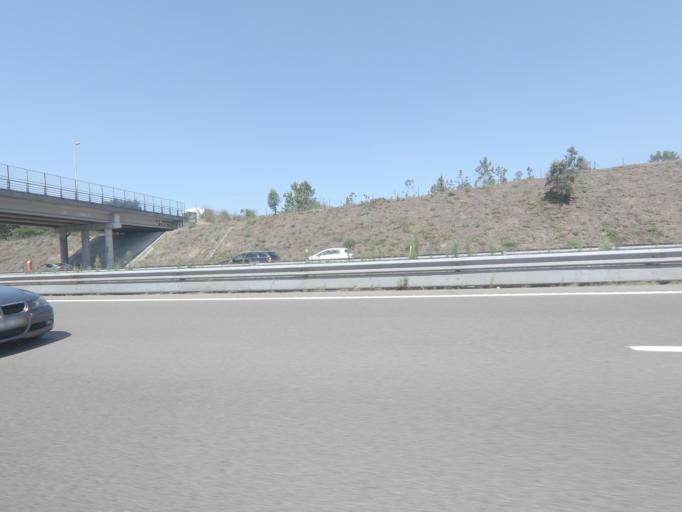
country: PT
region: Porto
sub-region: Matosinhos
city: Guifoes
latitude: 41.1980
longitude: -8.6613
